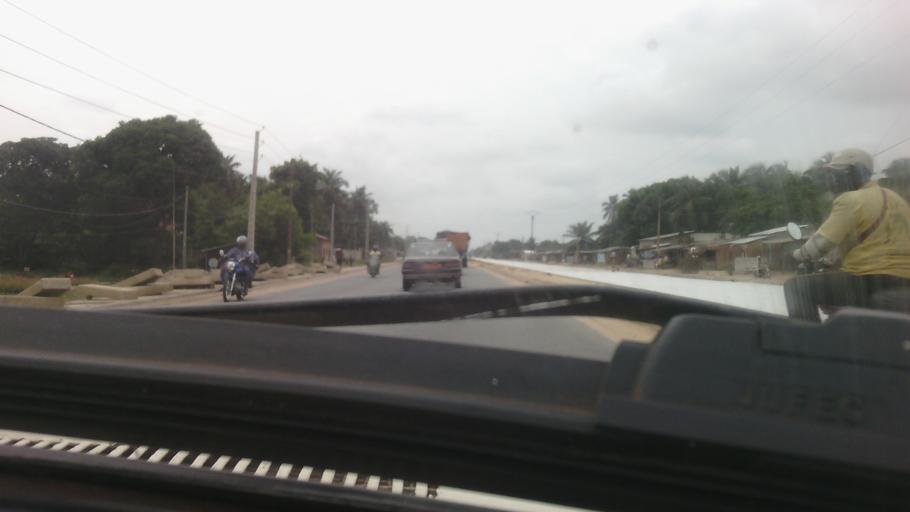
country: BJ
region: Atlantique
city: Hevie
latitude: 6.3832
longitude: 2.1856
